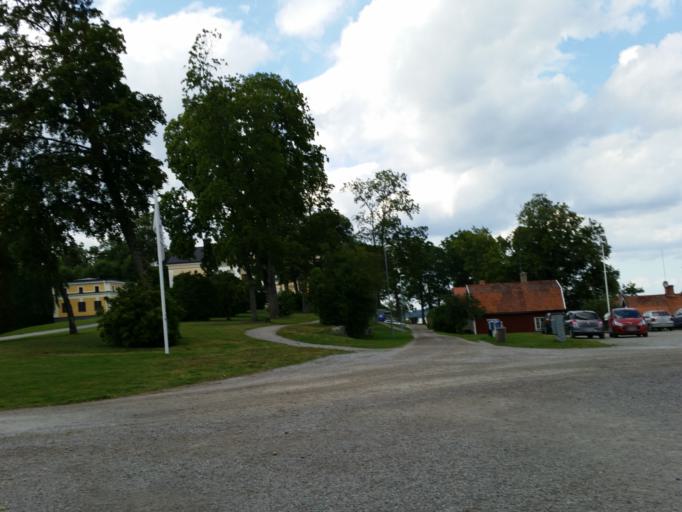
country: SE
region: Soedermanland
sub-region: Strangnas Kommun
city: Mariefred
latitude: 59.2452
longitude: 17.3112
